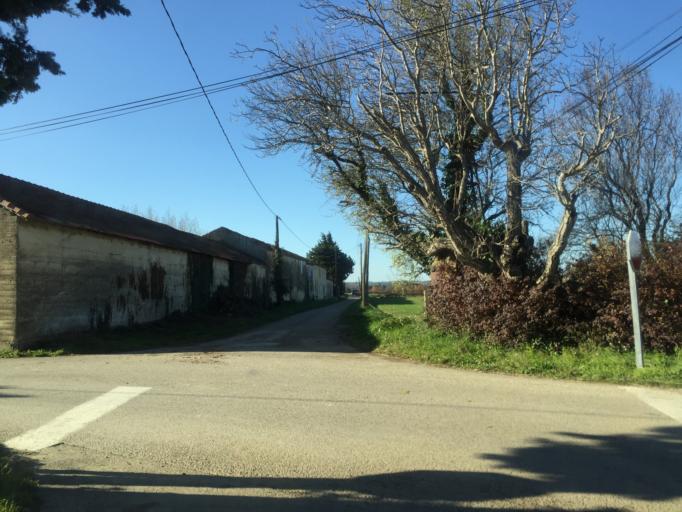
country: FR
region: Provence-Alpes-Cote d'Azur
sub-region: Departement du Vaucluse
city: Jonquieres
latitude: 44.0957
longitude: 4.9099
